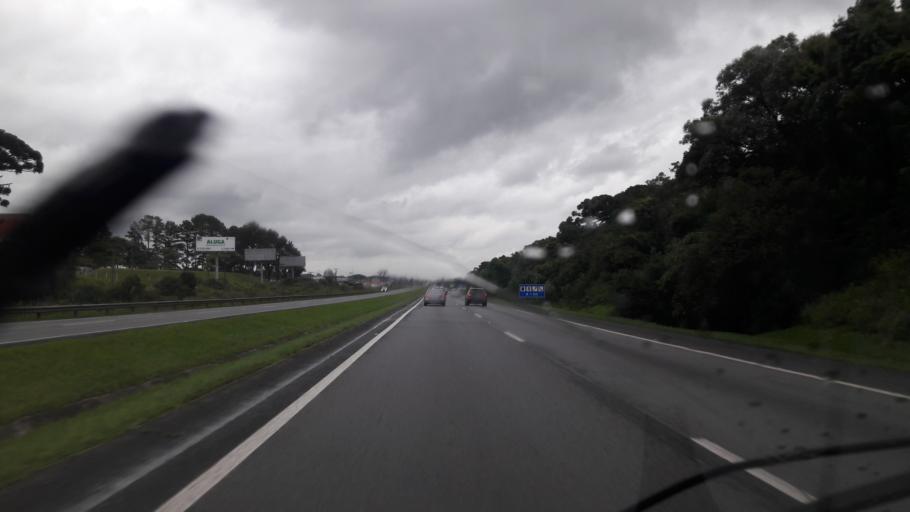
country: BR
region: Parana
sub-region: Piraquara
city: Piraquara
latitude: -25.5357
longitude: -49.0737
